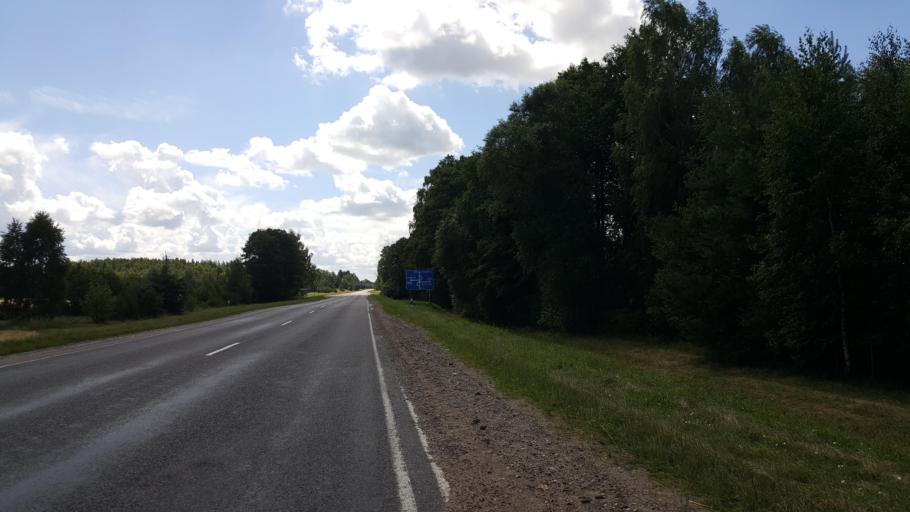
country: BY
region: Brest
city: Kamyanyets
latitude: 52.3472
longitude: 23.9024
